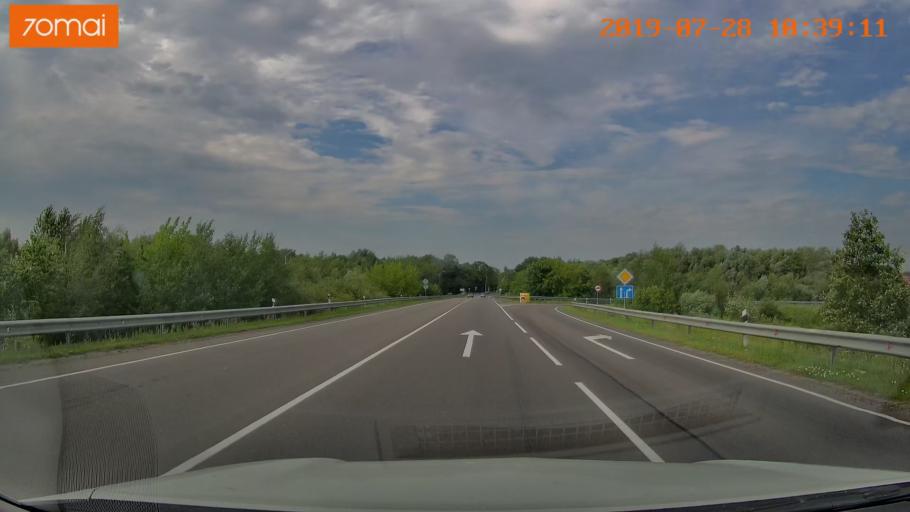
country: RU
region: Kaliningrad
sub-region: Gorod Kaliningrad
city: Kaliningrad
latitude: 54.7191
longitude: 20.3865
